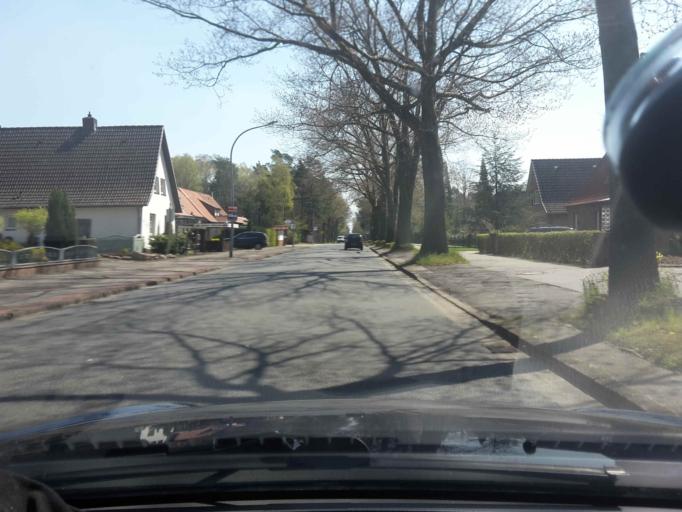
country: DE
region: Lower Saxony
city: Schneverdingen
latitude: 53.1087
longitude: 9.8108
